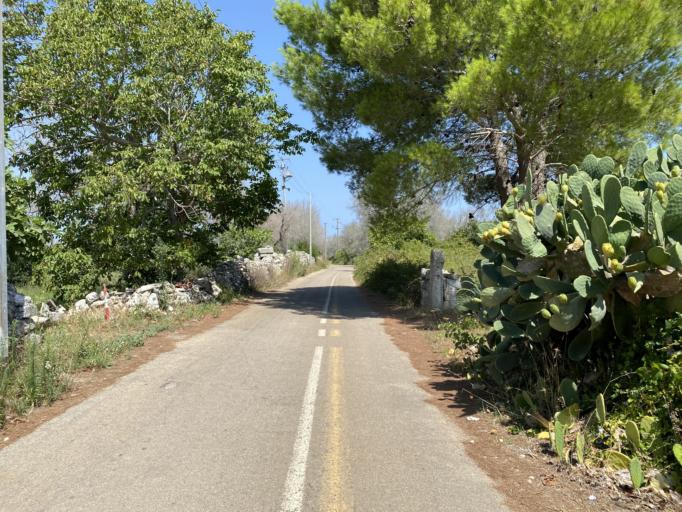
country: IT
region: Apulia
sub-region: Provincia di Lecce
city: Sanarica
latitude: 40.0967
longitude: 18.3538
